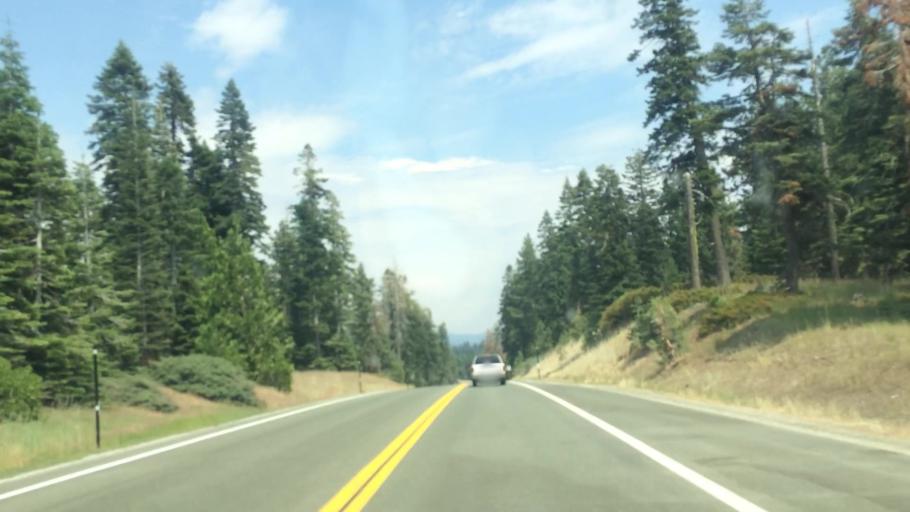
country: US
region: California
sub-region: Amador County
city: Pioneer
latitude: 38.5563
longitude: -120.2948
